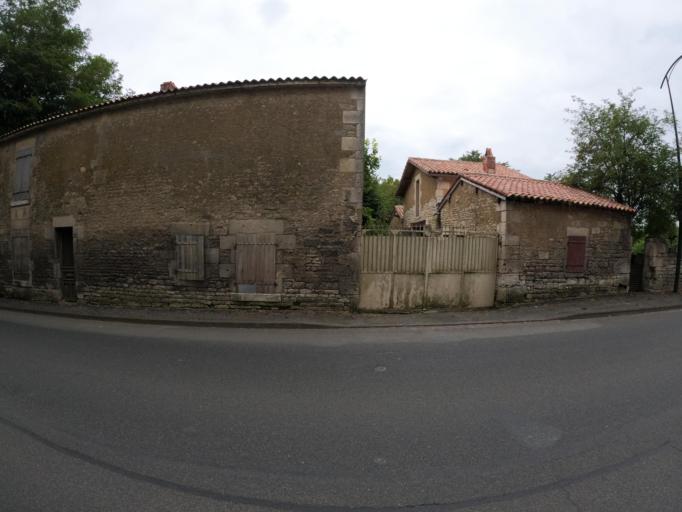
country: FR
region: Pays de la Loire
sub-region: Departement de la Vendee
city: Saint-Hilaire-des-Loges
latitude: 46.3989
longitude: -0.6612
